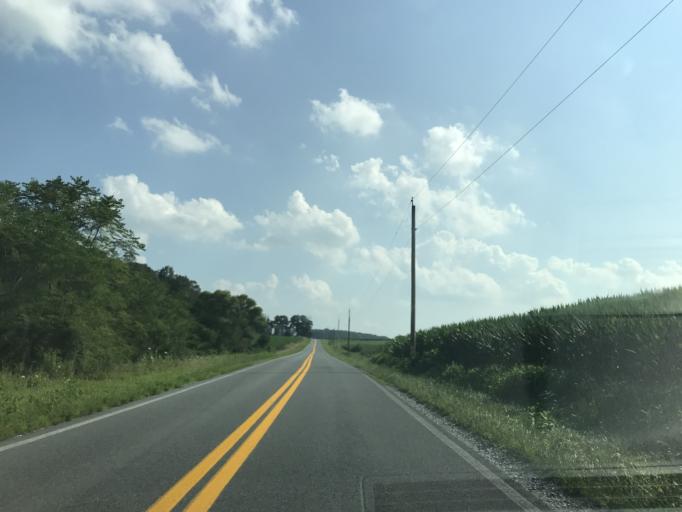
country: US
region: Maryland
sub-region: Carroll County
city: Manchester
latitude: 39.6483
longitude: -76.9365
